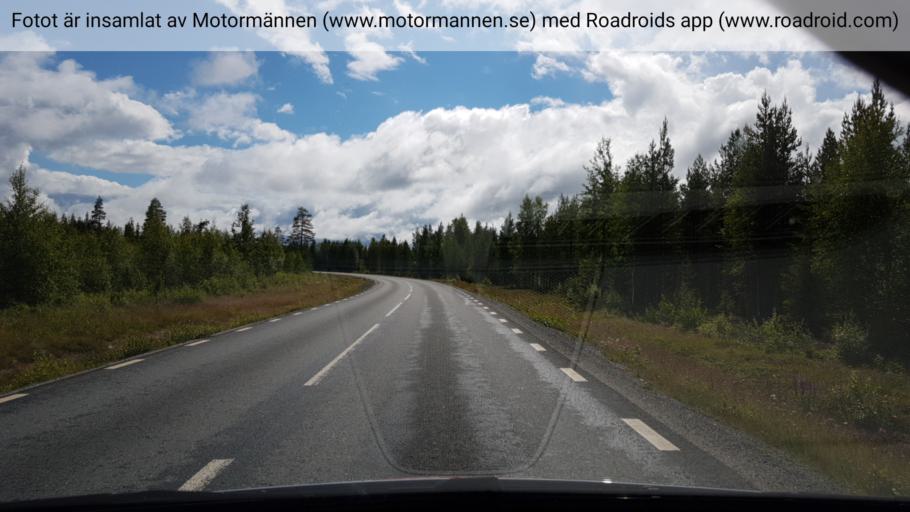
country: SE
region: Vaesterbotten
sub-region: Bjurholms Kommun
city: Bjurholm
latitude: 64.3410
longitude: 19.1466
